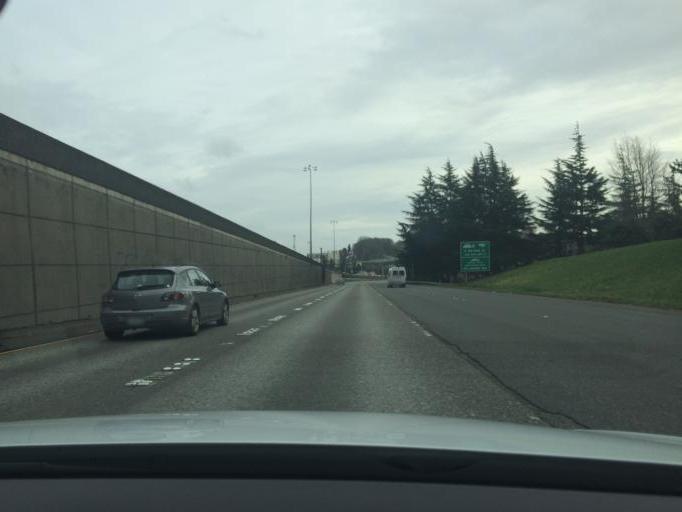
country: US
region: Washington
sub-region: King County
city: Seattle
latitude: 47.6013
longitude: -122.3246
